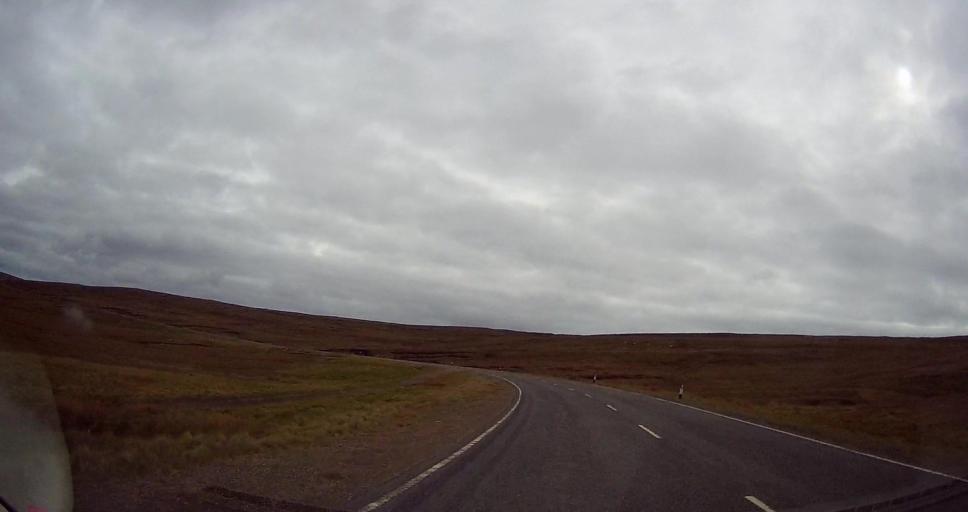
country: GB
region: Scotland
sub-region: Shetland Islands
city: Shetland
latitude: 60.6470
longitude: -1.0699
